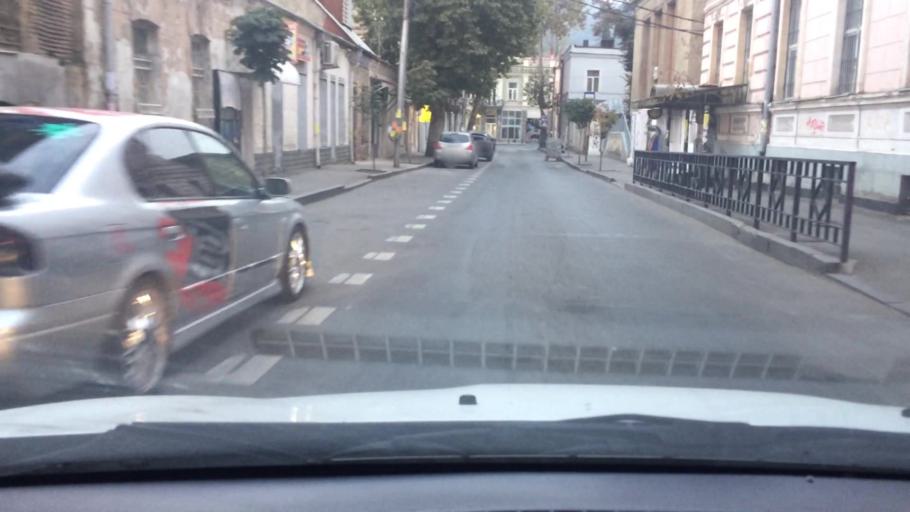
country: GE
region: T'bilisi
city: Tbilisi
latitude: 41.7064
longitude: 44.8012
